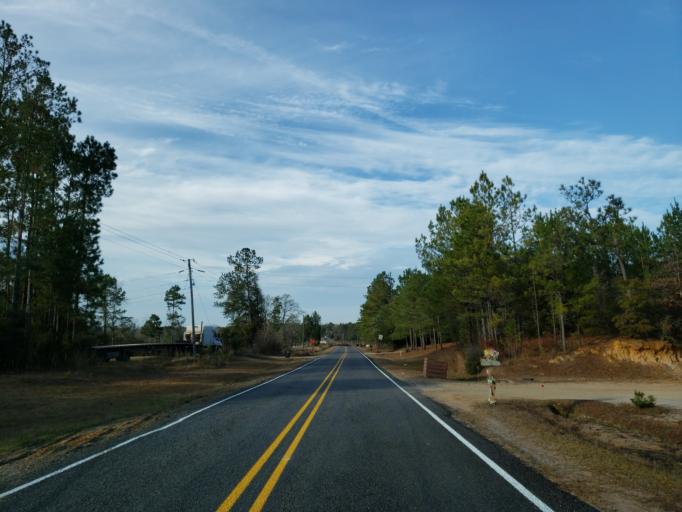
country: US
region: Mississippi
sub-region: Wayne County
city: Belmont
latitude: 31.4968
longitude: -88.5062
